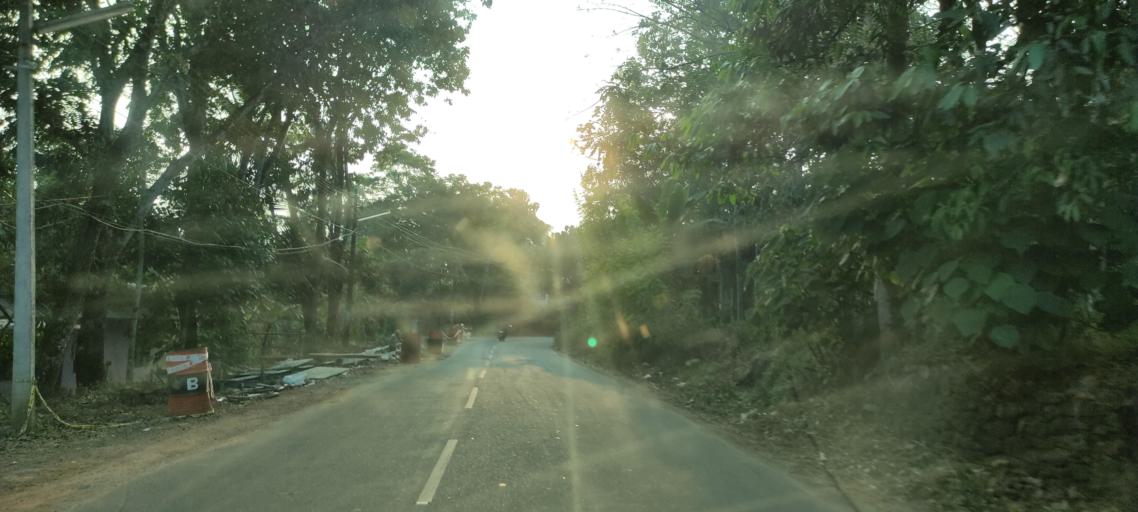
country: IN
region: Kerala
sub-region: Alappuzha
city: Mavelikara
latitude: 9.2501
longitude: 76.5731
